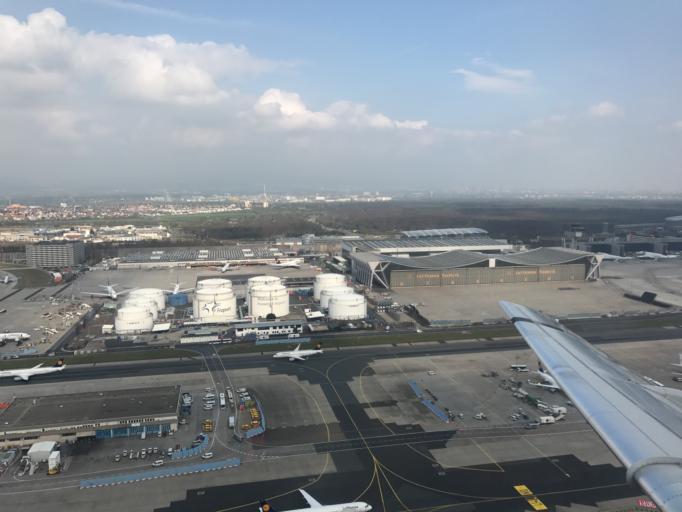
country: DE
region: Hesse
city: Kelsterbach
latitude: 50.0374
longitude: 8.5550
